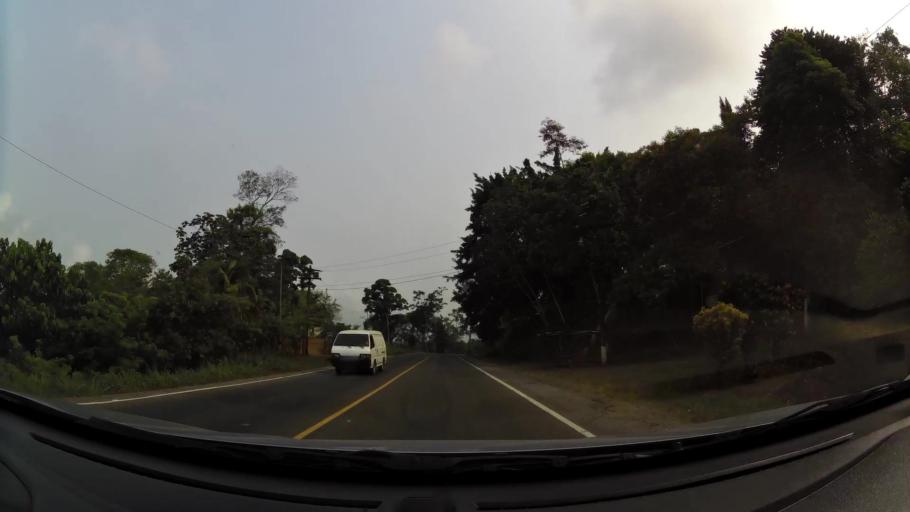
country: HN
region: Atlantida
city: Mezapa
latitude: 15.5873
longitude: -87.6112
